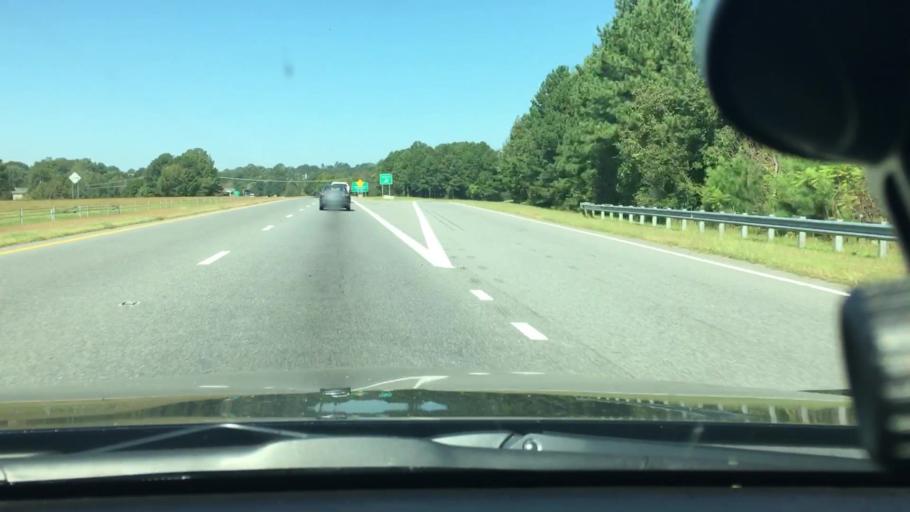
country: US
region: North Carolina
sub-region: Cleveland County
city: Kings Mountain
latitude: 35.2449
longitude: -81.3263
